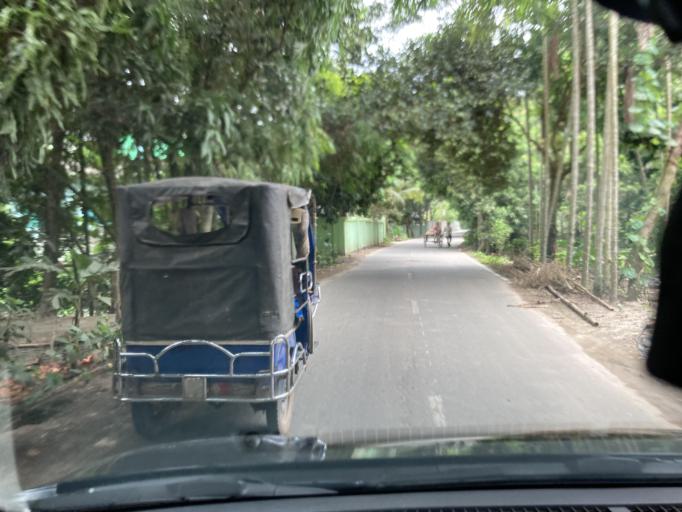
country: BD
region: Dhaka
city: Dohar
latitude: 23.7891
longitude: 90.0623
